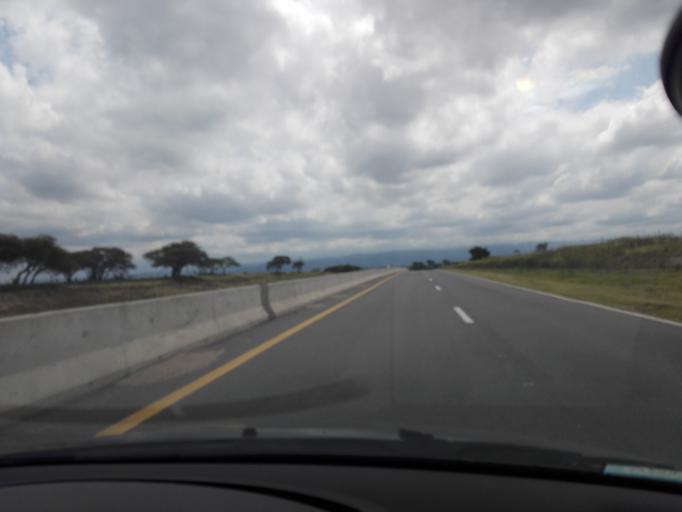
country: AR
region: Cordoba
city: Alta Gracia
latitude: -31.6522
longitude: -64.3257
